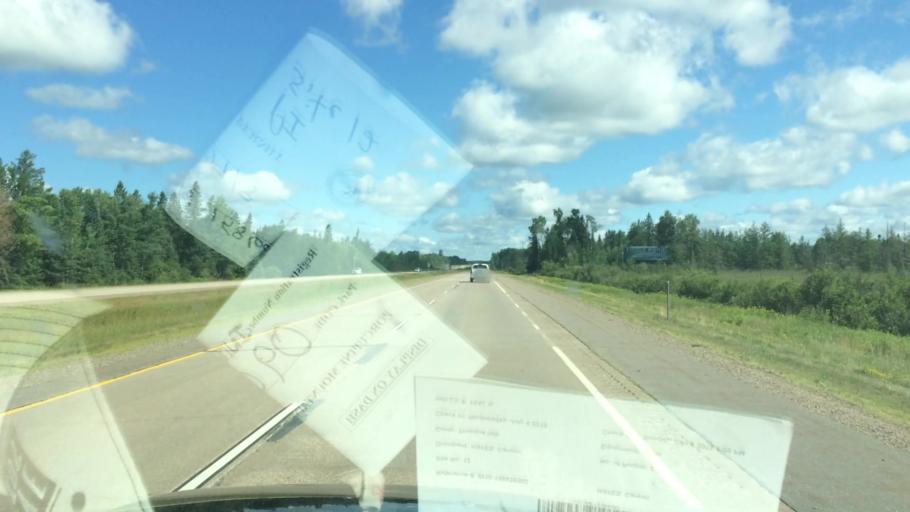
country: US
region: Wisconsin
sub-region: Lincoln County
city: Tomahawk
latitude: 45.3862
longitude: -89.6722
